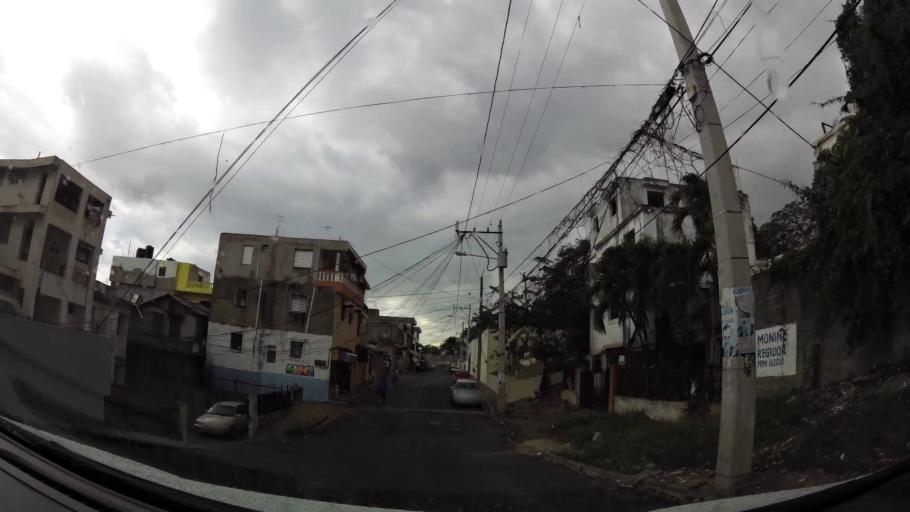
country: DO
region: Nacional
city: La Agustina
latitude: 18.5006
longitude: -69.9338
